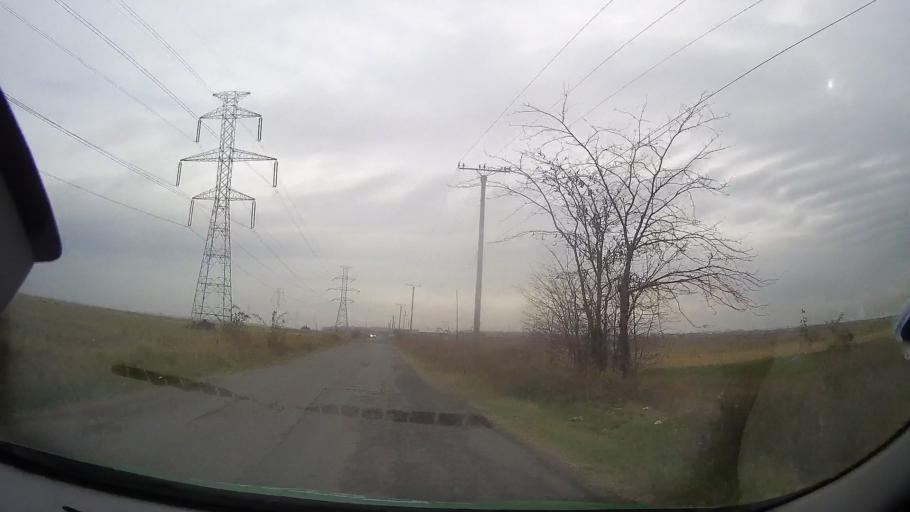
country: RO
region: Prahova
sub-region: Comuna Valea Calugareasca
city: Pantazi
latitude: 44.9281
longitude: 26.1491
